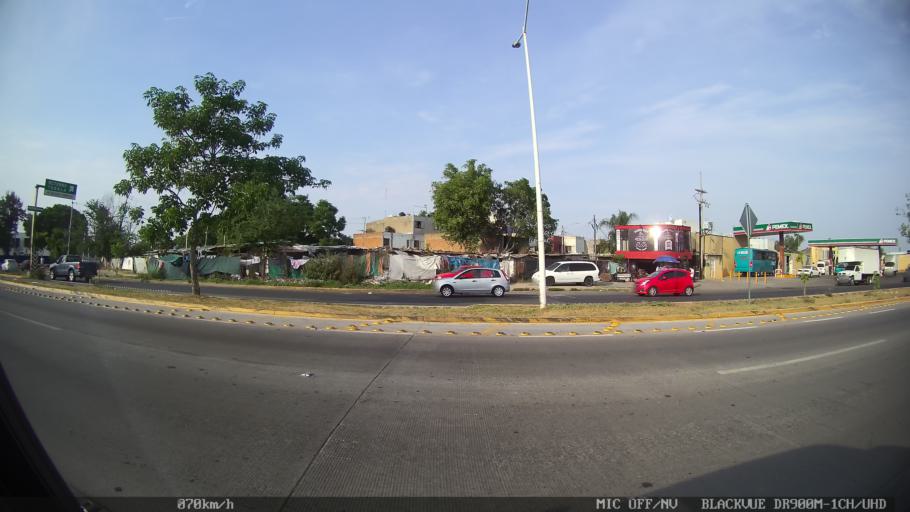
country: MX
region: Jalisco
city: Tlaquepaque
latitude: 20.7145
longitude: -103.3038
